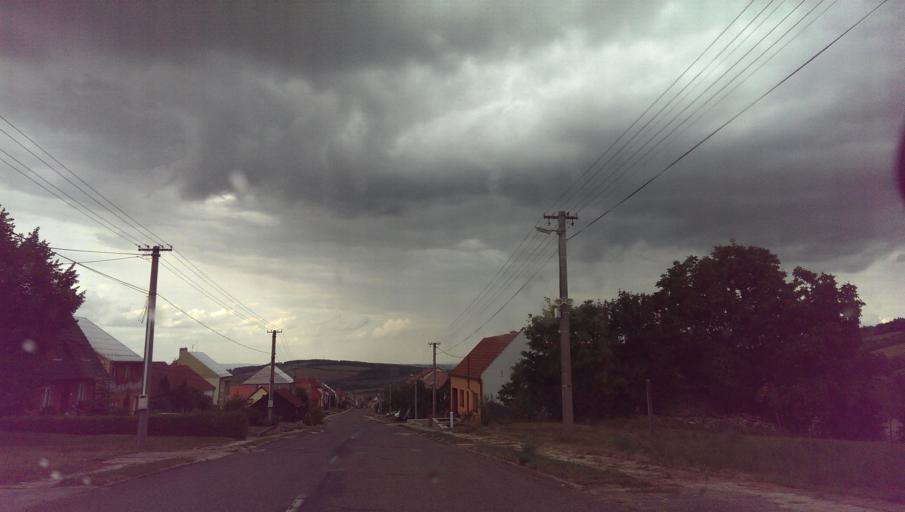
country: CZ
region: South Moravian
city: Velka nad Velickou
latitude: 48.9041
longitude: 17.5643
